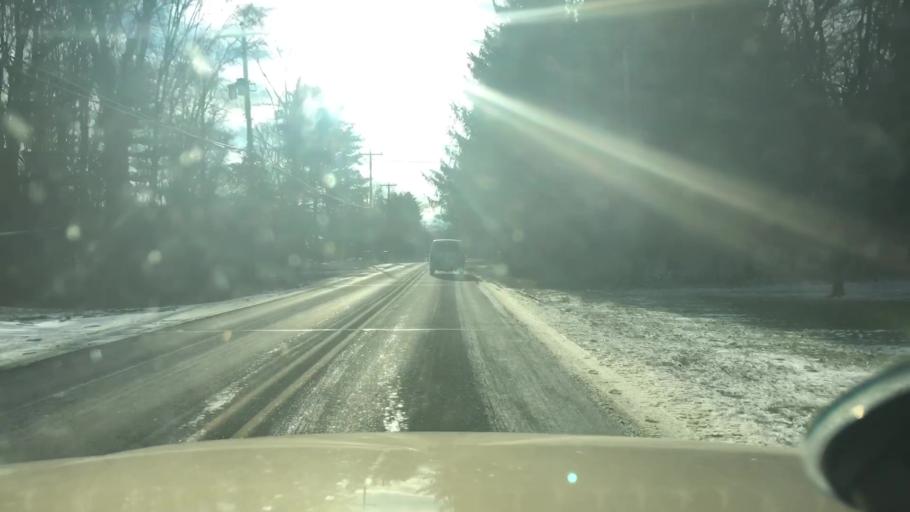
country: US
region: Michigan
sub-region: Jackson County
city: Vandercook Lake
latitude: 42.1970
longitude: -84.4447
